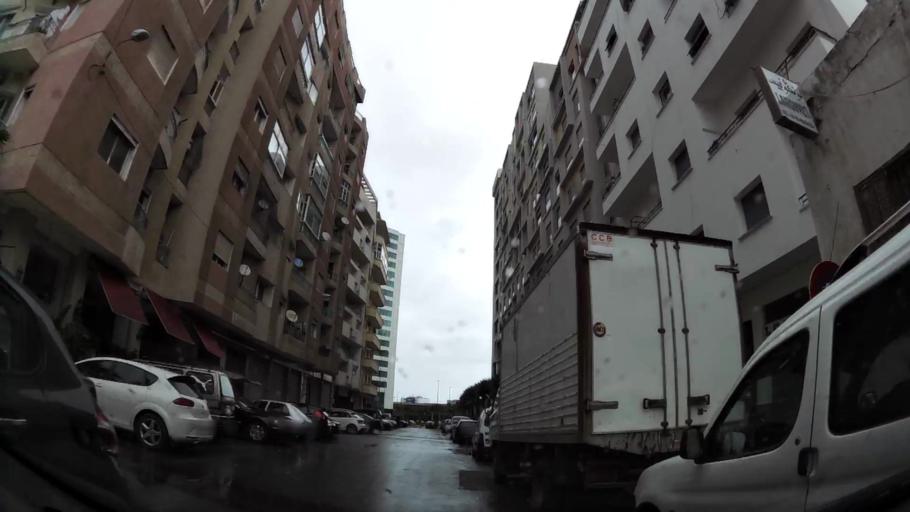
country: MA
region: Grand Casablanca
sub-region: Casablanca
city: Casablanca
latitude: 33.5937
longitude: -7.6008
